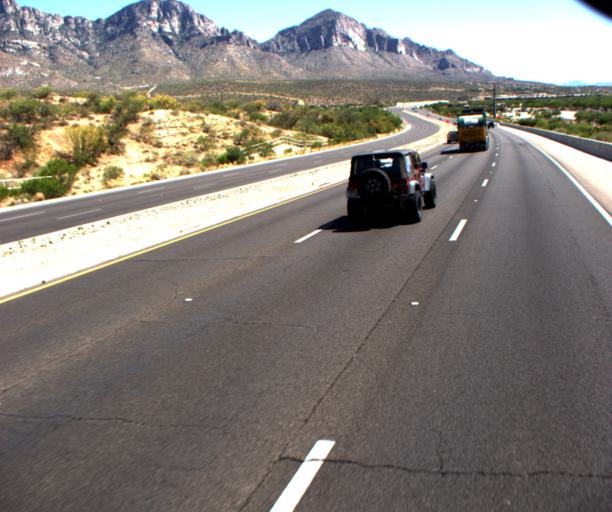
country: US
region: Arizona
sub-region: Pima County
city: Oro Valley
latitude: 32.4236
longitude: -110.9363
